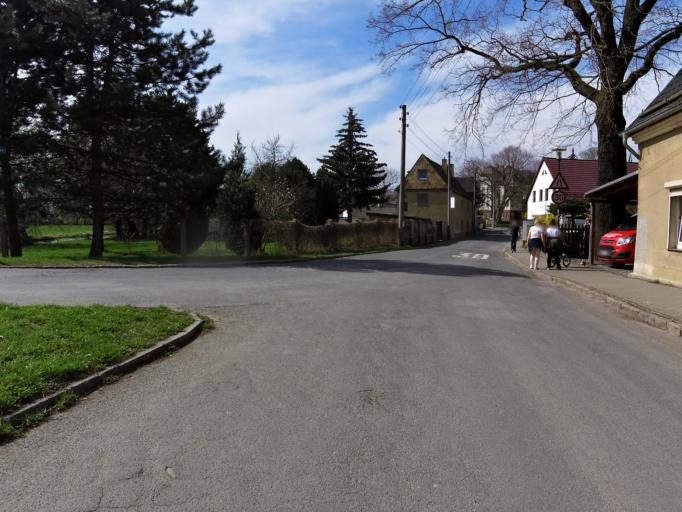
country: DE
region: Saxony
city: Schkeuditz
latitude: 51.3826
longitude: 12.2729
